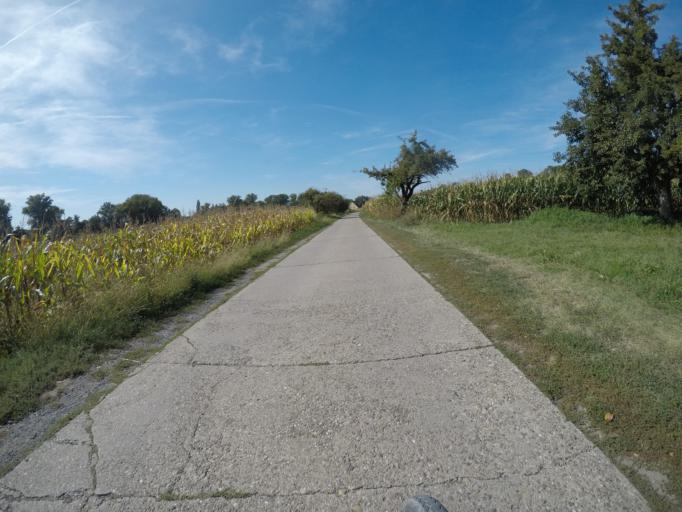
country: DE
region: Baden-Wuerttemberg
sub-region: Karlsruhe Region
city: Ubstadt-Weiher
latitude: 49.1489
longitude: 8.6627
